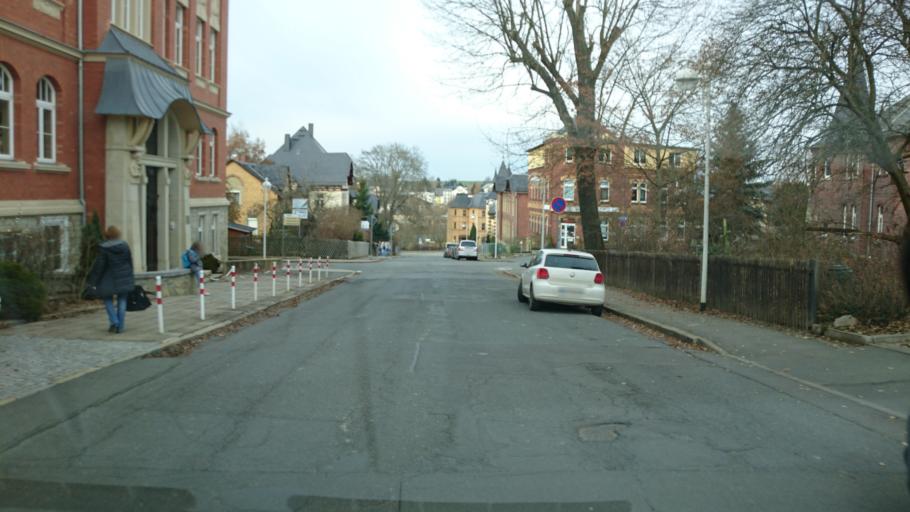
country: DE
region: Thuringia
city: Schleiz
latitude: 50.5781
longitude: 11.8155
